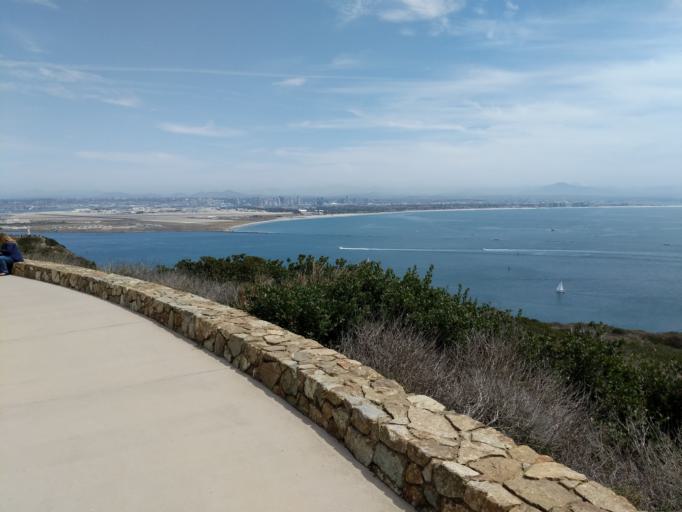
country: US
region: California
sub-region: San Diego County
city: Coronado
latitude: 32.6718
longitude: -117.2406
